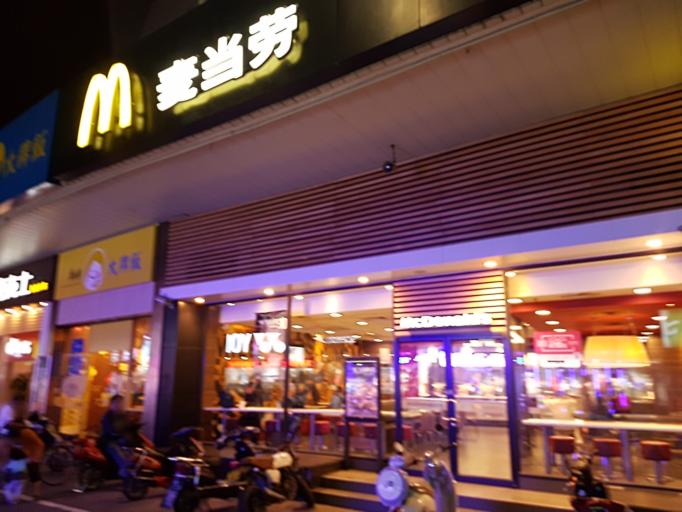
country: CN
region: Shanghai Shi
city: Xuhui
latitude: 31.1822
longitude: 121.4384
